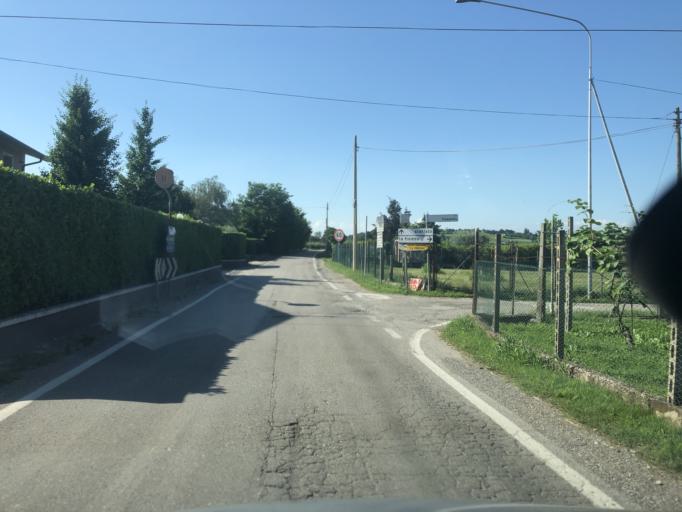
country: IT
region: Veneto
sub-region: Provincia di Verona
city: Villafranca di Verona
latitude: 45.3780
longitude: 10.8265
